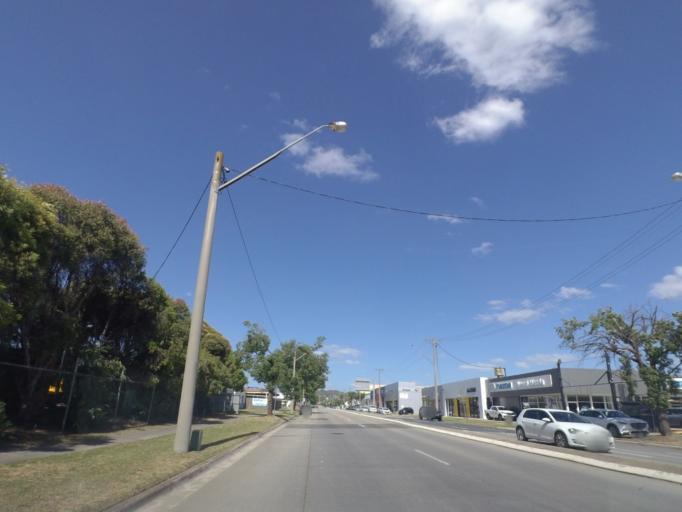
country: AU
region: New South Wales
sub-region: Albury Municipality
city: South Albury
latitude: -36.0842
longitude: 146.9100
